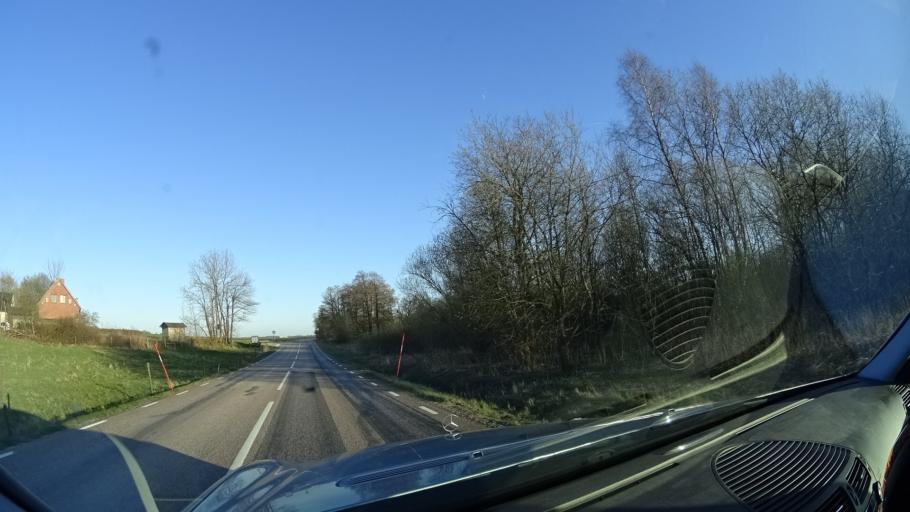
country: SE
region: Skane
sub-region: Bjuvs Kommun
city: Billesholm
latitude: 56.0265
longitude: 13.0434
